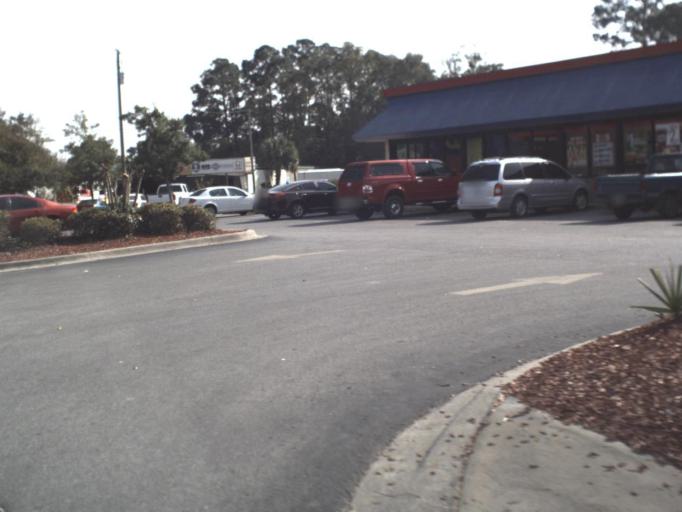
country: US
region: Florida
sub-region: Bay County
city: Springfield
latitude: 30.1538
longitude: -85.6178
